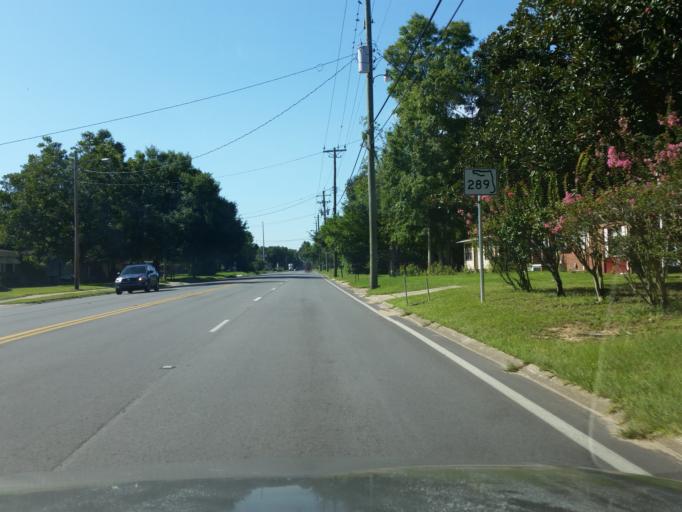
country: US
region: Florida
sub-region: Escambia County
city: Goulding
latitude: 30.4470
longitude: -87.2126
